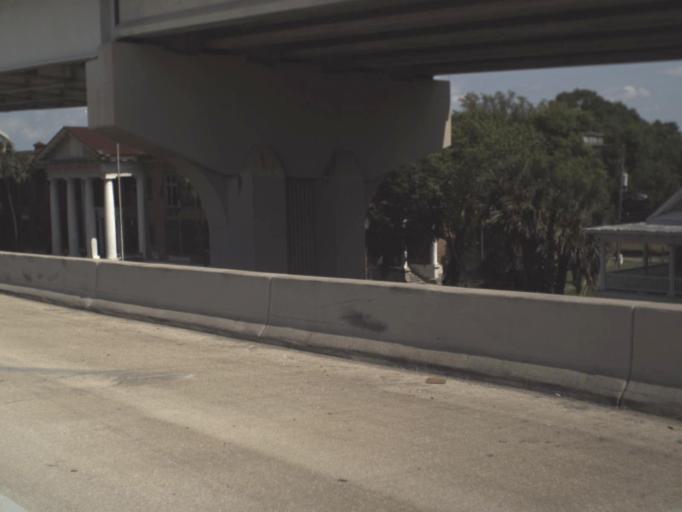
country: US
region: Florida
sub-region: Duval County
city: Jacksonville
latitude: 30.3183
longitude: -81.6798
